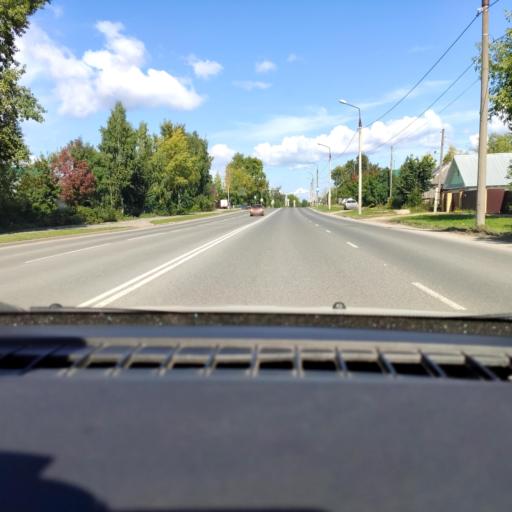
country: RU
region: Perm
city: Polazna
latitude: 58.1211
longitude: 56.4035
